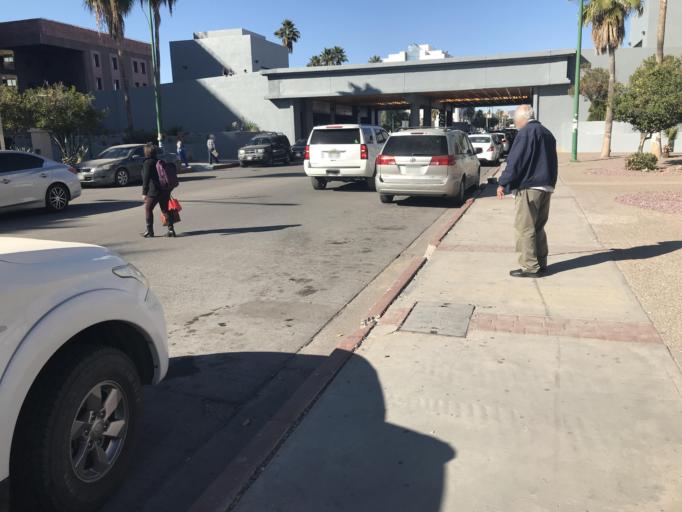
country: MX
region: Sonora
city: Hermosillo
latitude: 29.0675
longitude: -110.9577
